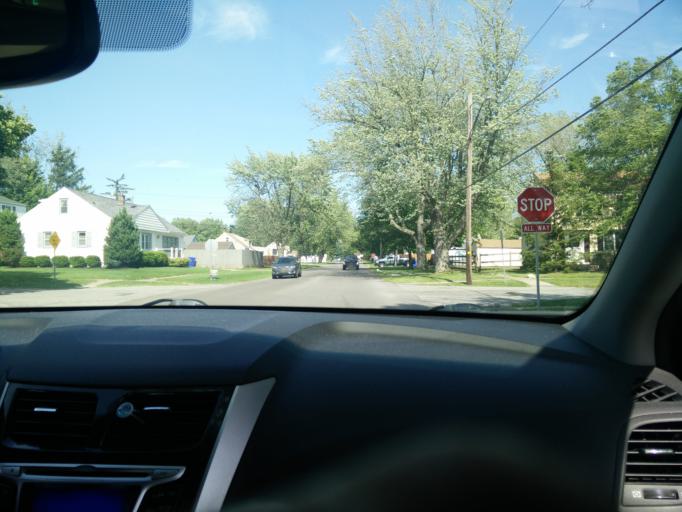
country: US
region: New York
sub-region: Erie County
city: West Seneca
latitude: 42.8319
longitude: -78.7978
